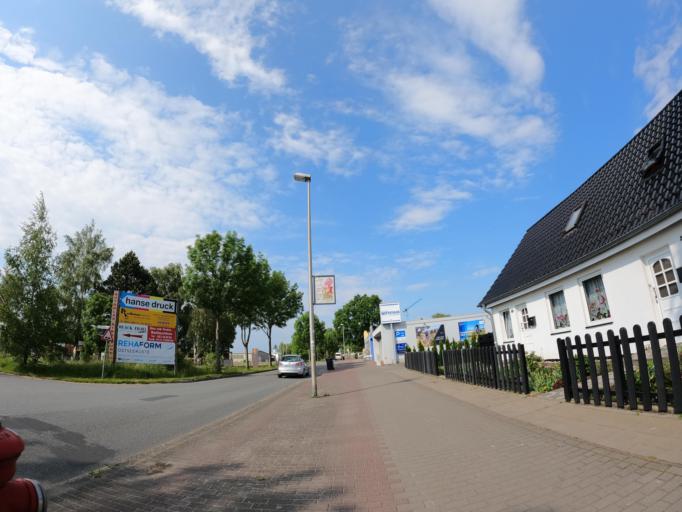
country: DE
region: Mecklenburg-Vorpommern
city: Stralsund
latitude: 54.3020
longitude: 13.0629
